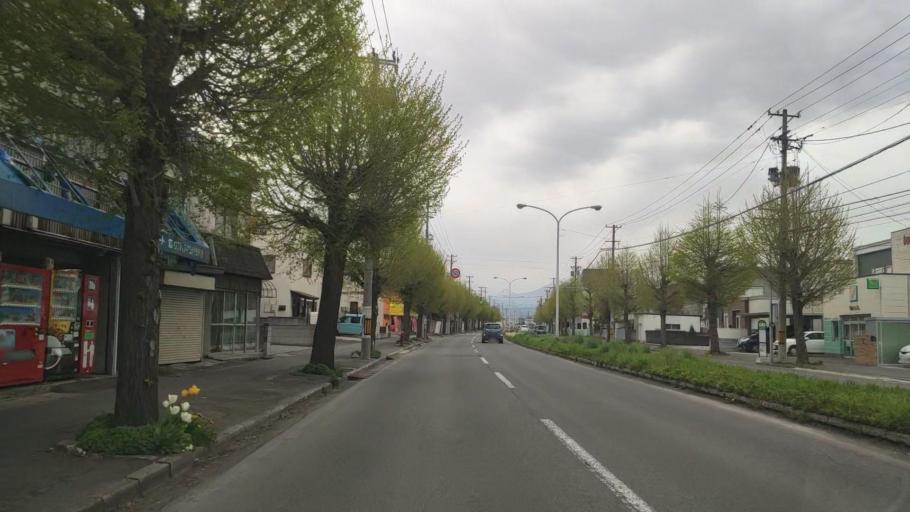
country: JP
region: Aomori
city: Aomori Shi
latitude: 40.8211
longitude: 140.7715
